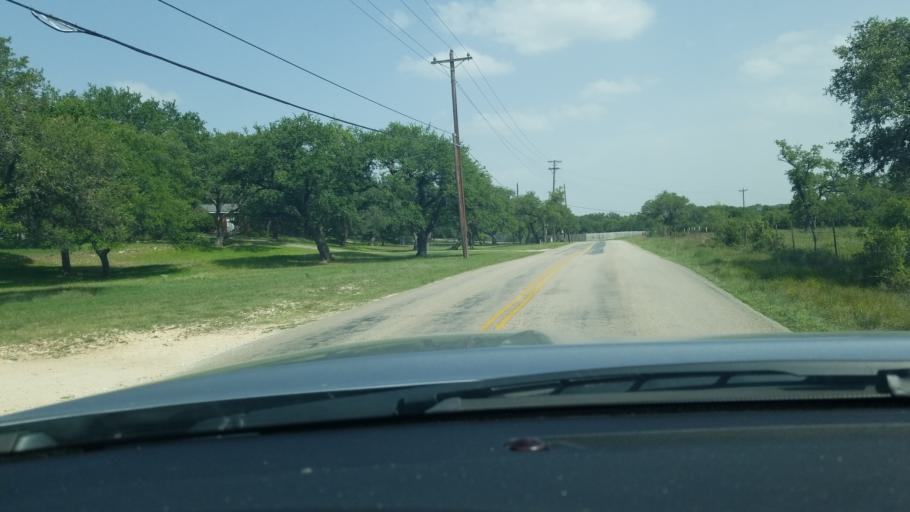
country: US
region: Texas
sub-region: Comal County
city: Bulverde
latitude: 29.7767
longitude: -98.4595
